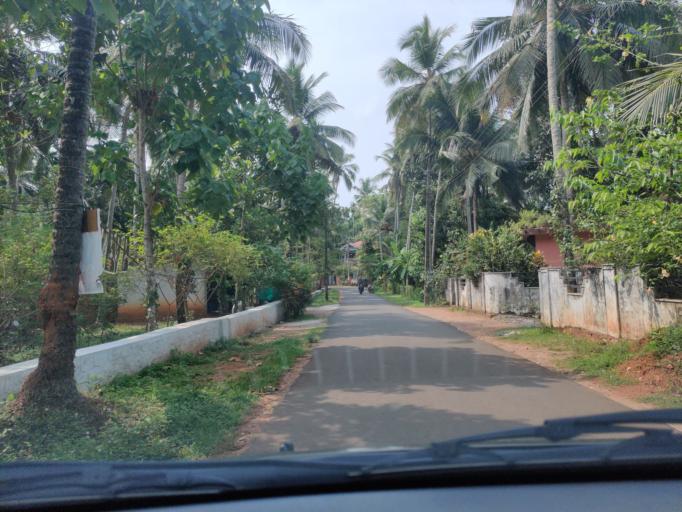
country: IN
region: Kerala
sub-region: Kozhikode
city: Kunnamangalam
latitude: 11.4190
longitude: 75.8733
